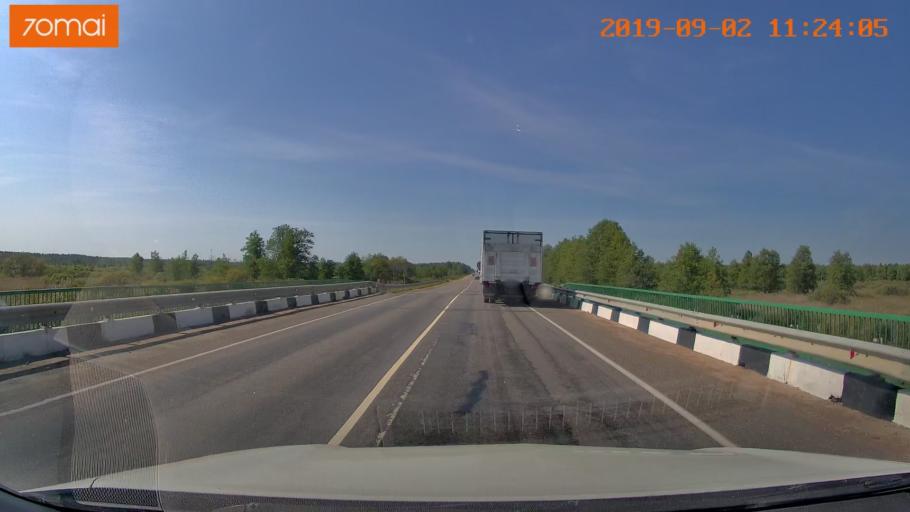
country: RU
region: Smolensk
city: Roslavl'
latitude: 54.0128
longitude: 32.9812
